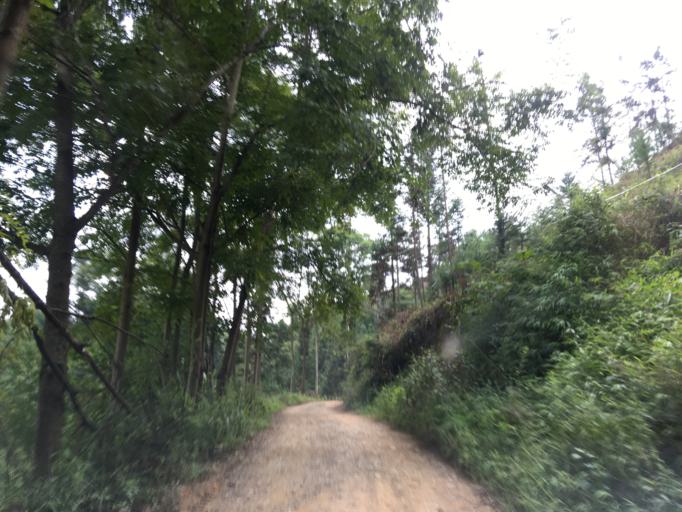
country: CN
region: Guangxi Zhuangzu Zizhiqu
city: Xinzhou
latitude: 24.8872
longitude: 105.8398
